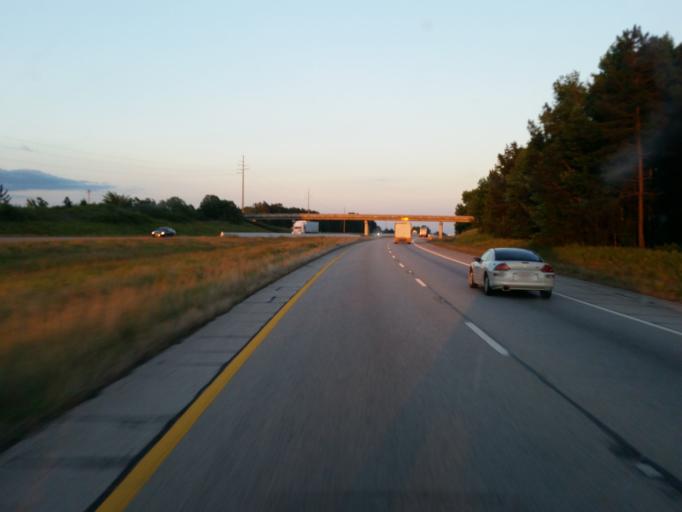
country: US
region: Texas
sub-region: Smith County
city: Hideaway
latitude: 32.4796
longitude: -95.4901
